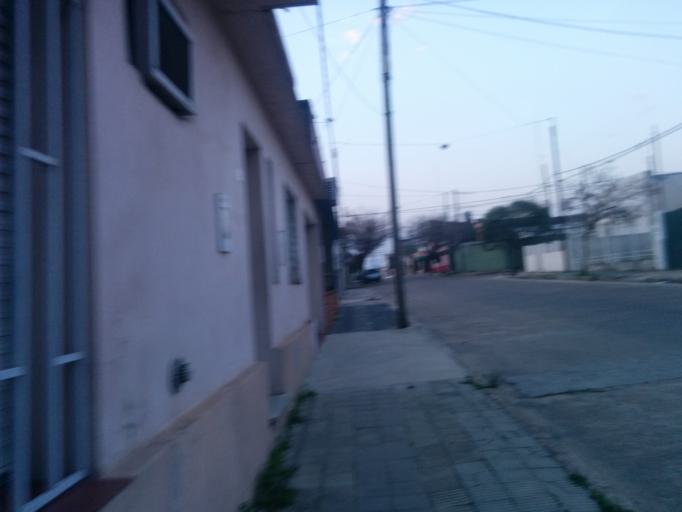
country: AR
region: Entre Rios
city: Concordia
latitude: -31.3877
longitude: -58.0210
